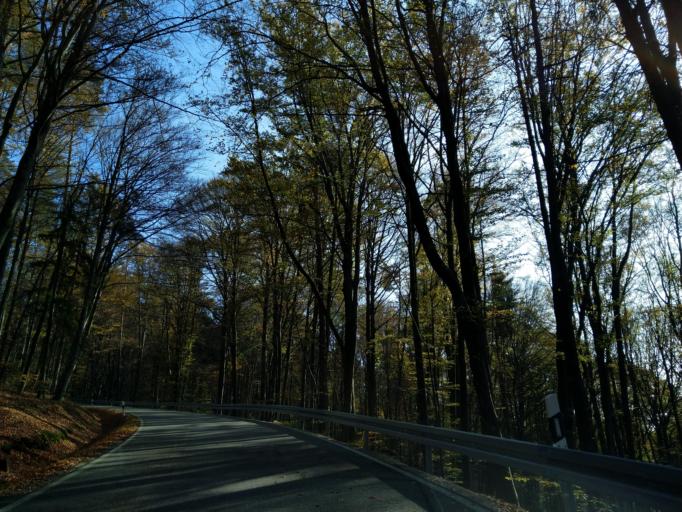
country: DE
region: Bavaria
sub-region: Lower Bavaria
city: Grattersdorf
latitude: 48.7941
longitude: 13.1837
